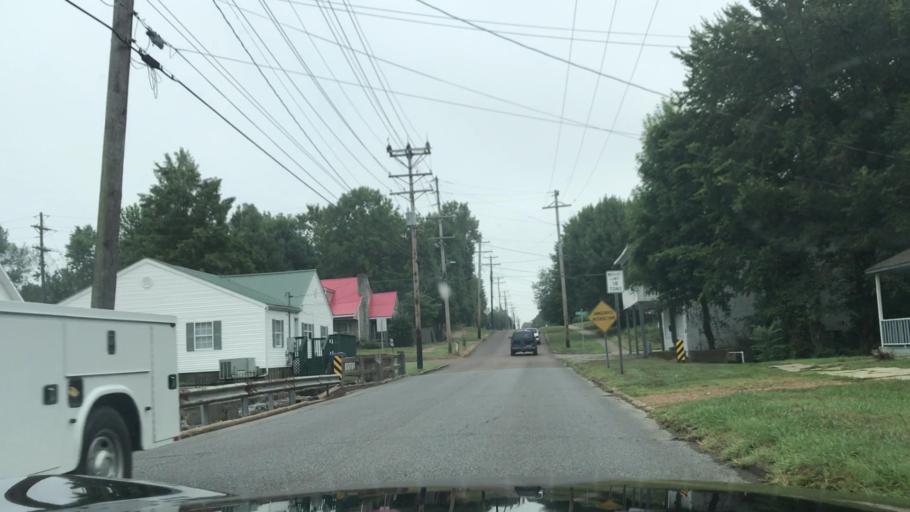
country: US
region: Kentucky
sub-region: Graves County
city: Mayfield
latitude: 36.7351
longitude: -88.6388
